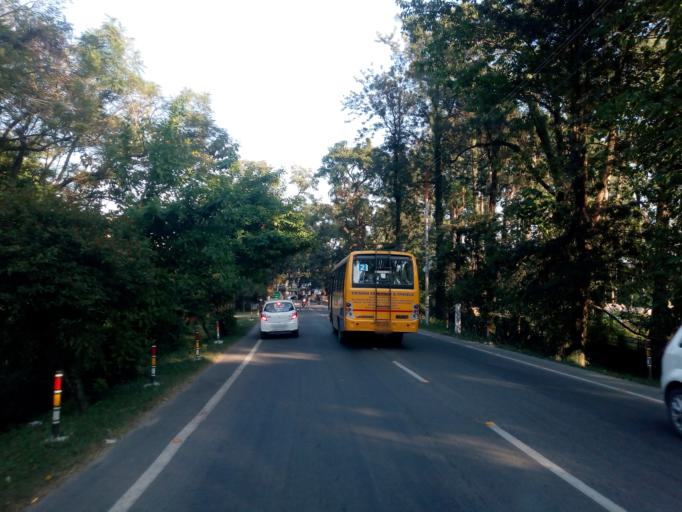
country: IN
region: Uttarakhand
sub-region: Dehradun
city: Dehradun
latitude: 30.3504
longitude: 78.0439
